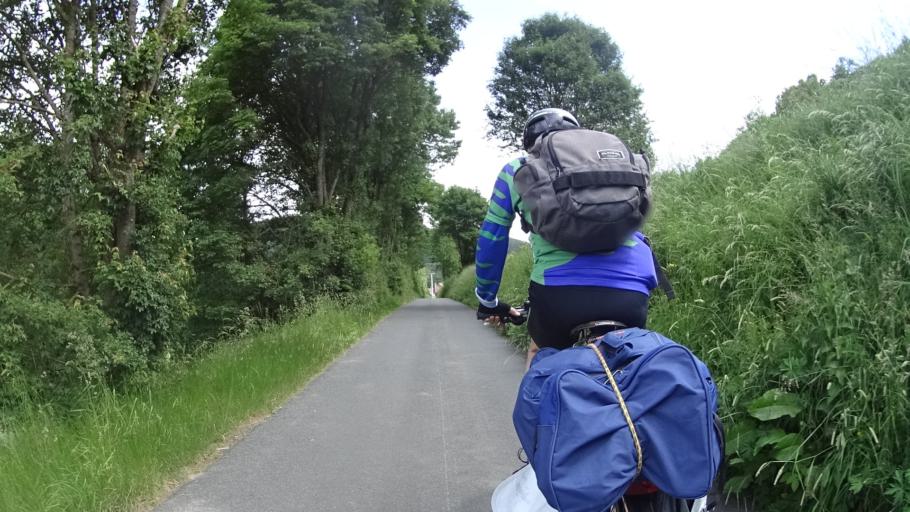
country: DE
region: Bavaria
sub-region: Regierungsbezirk Unterfranken
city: Neunkirchen
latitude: 49.6707
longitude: 9.3869
